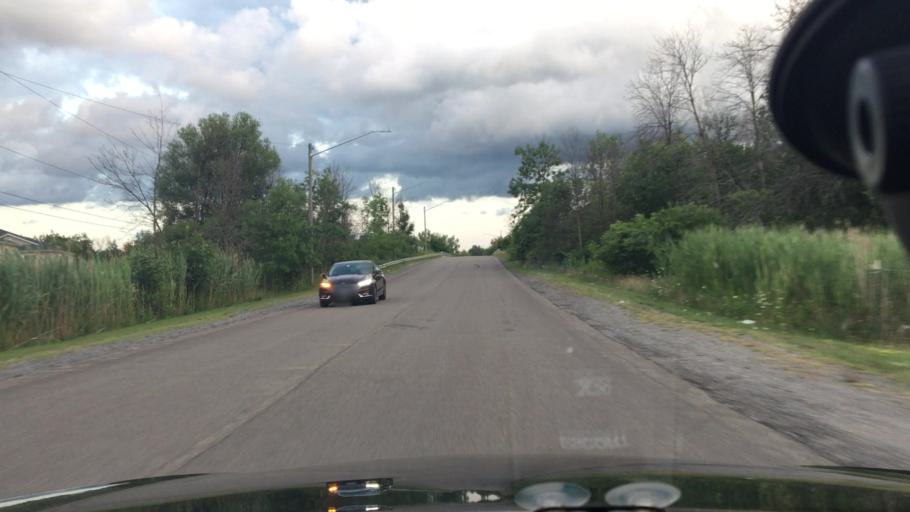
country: US
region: New York
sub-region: Erie County
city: West Seneca
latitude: 42.8454
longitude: -78.7648
